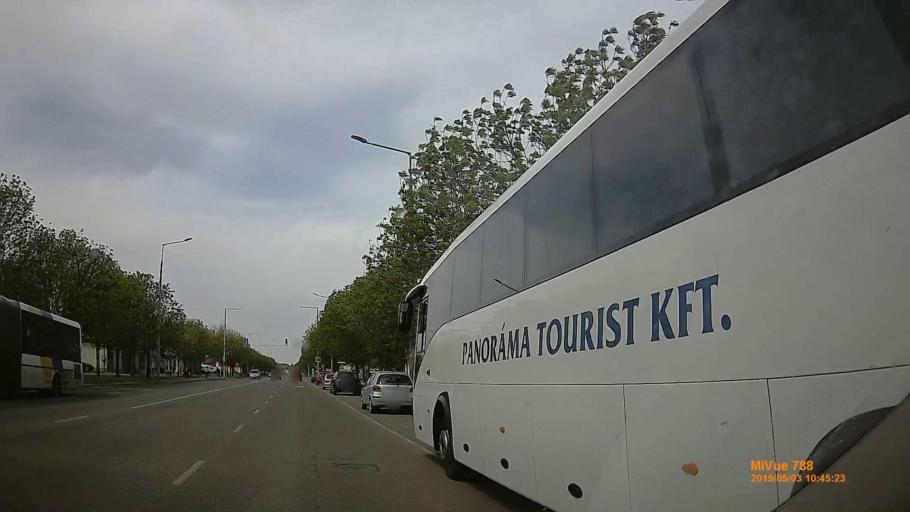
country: HU
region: Jasz-Nagykun-Szolnok
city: Szolnok
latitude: 47.1941
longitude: 20.1885
